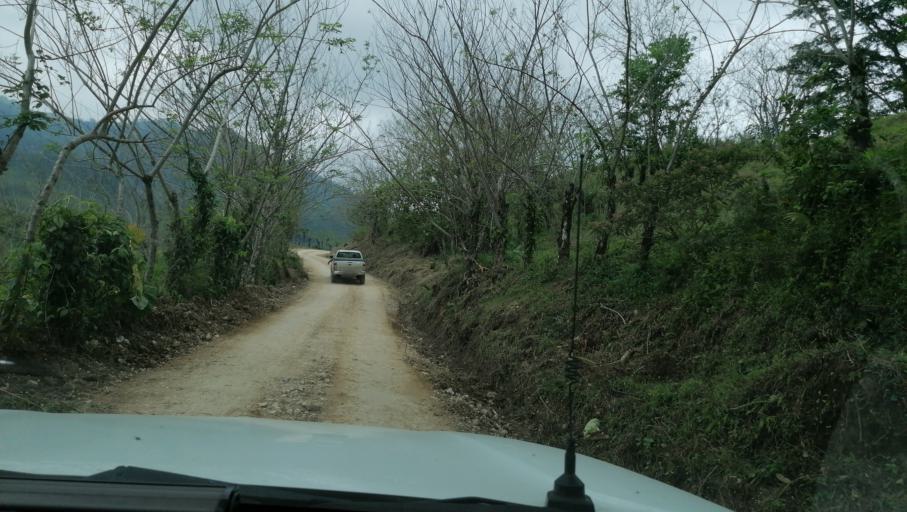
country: MX
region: Chiapas
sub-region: Ocotepec
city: San Pablo Huacano
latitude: 17.2684
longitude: -93.2565
